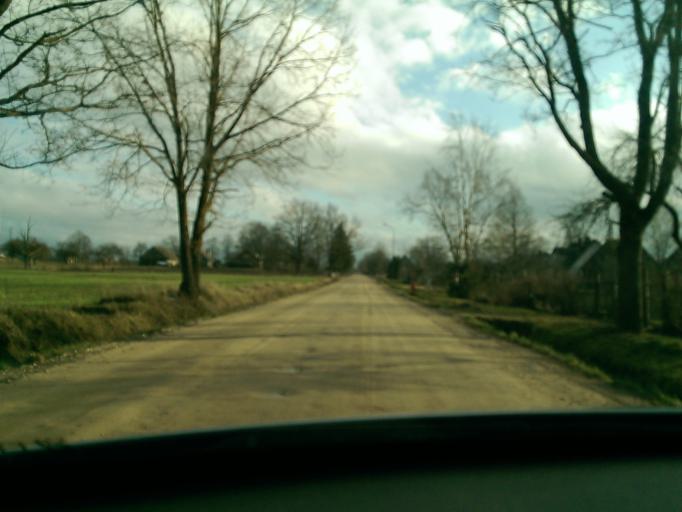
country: LV
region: Kuldigas Rajons
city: Kuldiga
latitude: 56.9762
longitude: 21.9888
